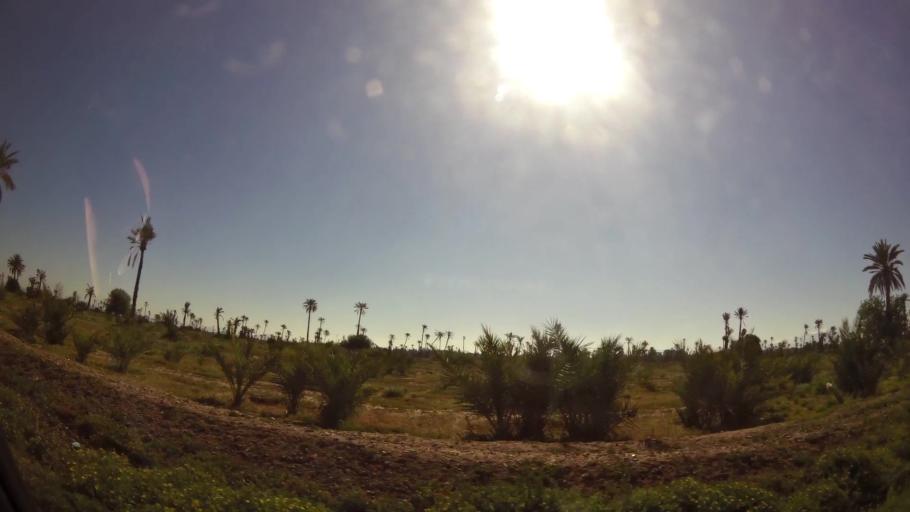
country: MA
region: Marrakech-Tensift-Al Haouz
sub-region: Marrakech
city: Marrakesh
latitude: 31.6625
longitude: -7.9534
